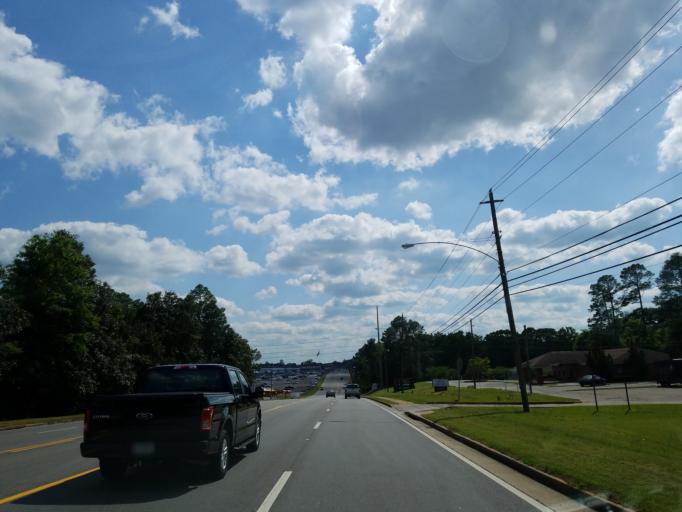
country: US
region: Georgia
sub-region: Peach County
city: Fort Valley
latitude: 32.5657
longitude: -83.8771
